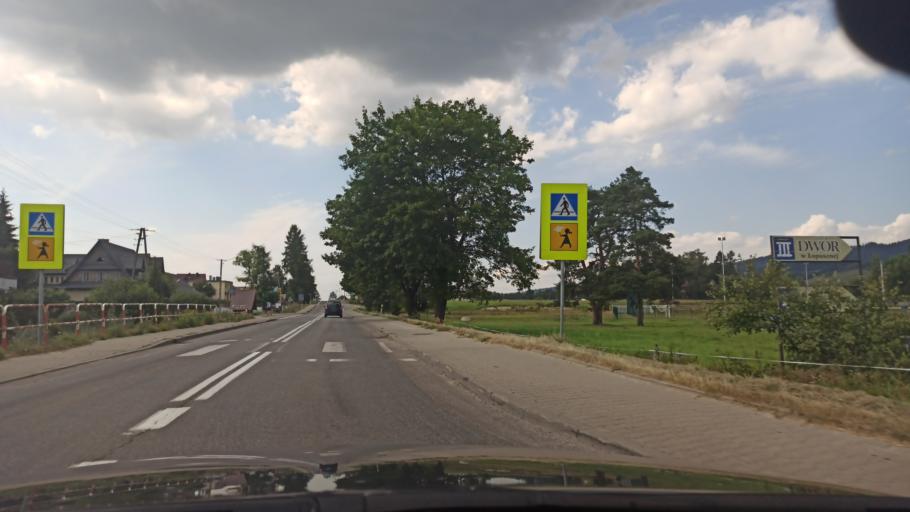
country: PL
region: Lesser Poland Voivodeship
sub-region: Powiat nowotarski
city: Lopuszna
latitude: 49.4714
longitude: 20.1258
